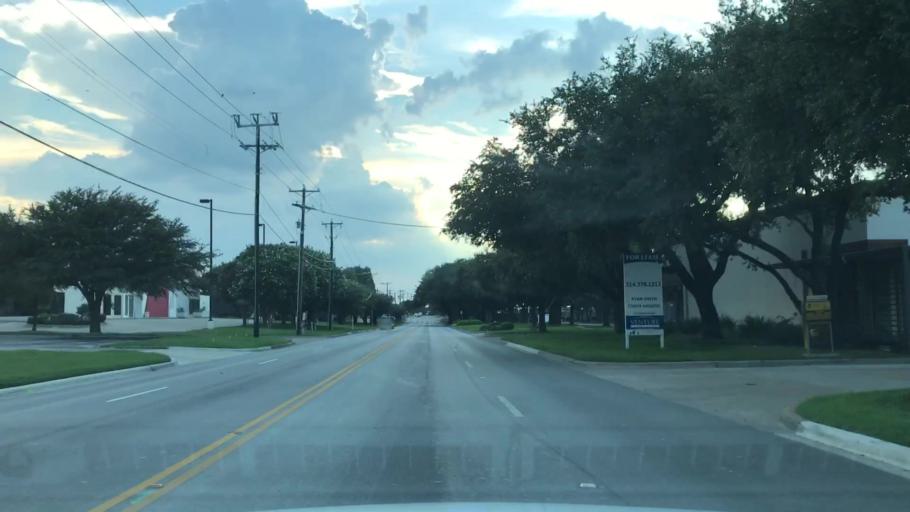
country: US
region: Texas
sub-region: Dallas County
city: Addison
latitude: 32.9331
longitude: -96.8262
